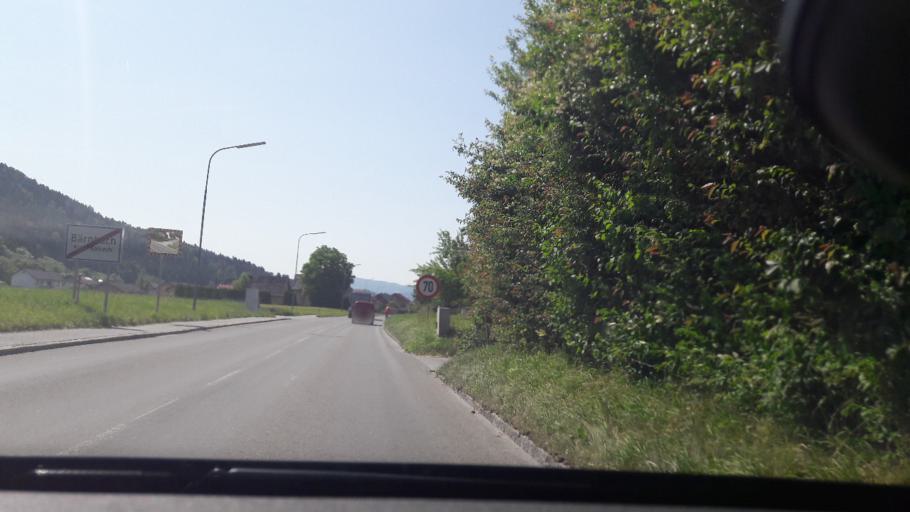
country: AT
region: Styria
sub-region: Politischer Bezirk Voitsberg
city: Kohlschwarz
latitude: 47.0912
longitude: 15.1212
